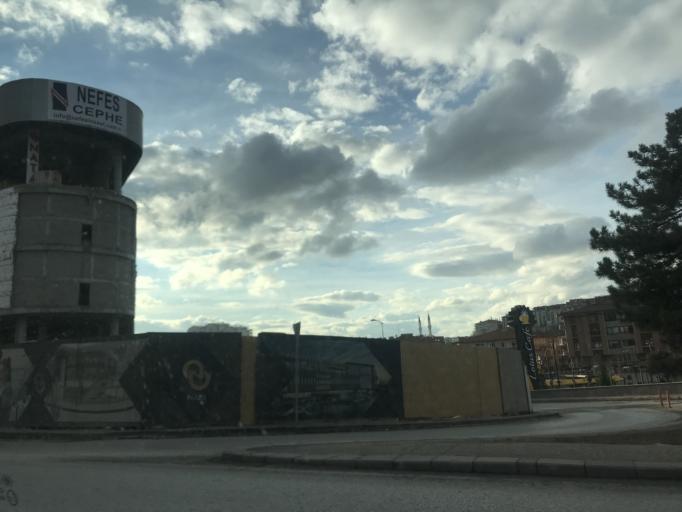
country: TR
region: Ankara
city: Mamak
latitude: 39.9764
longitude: 32.8853
